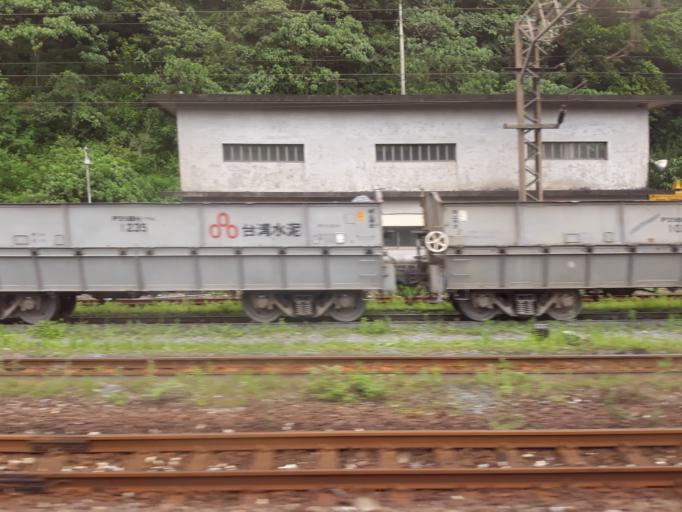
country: TW
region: Taiwan
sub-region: Yilan
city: Yilan
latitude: 24.5702
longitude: 121.8450
